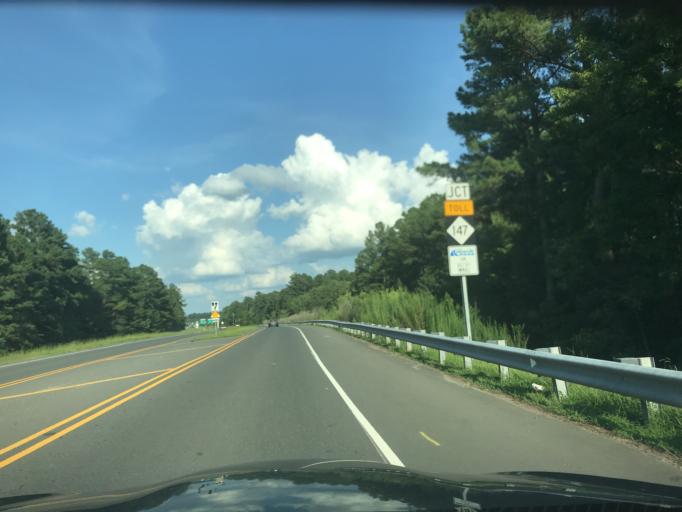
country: US
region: North Carolina
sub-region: Wake County
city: Morrisville
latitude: 35.8755
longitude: -78.8760
